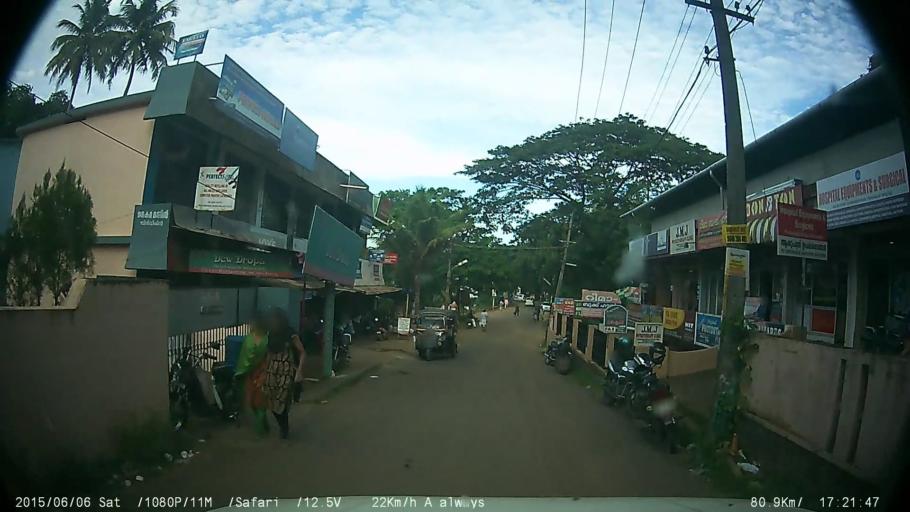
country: IN
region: Kerala
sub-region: Pattanamtitta
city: Tiruvalla
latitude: 9.3842
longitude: 76.5773
